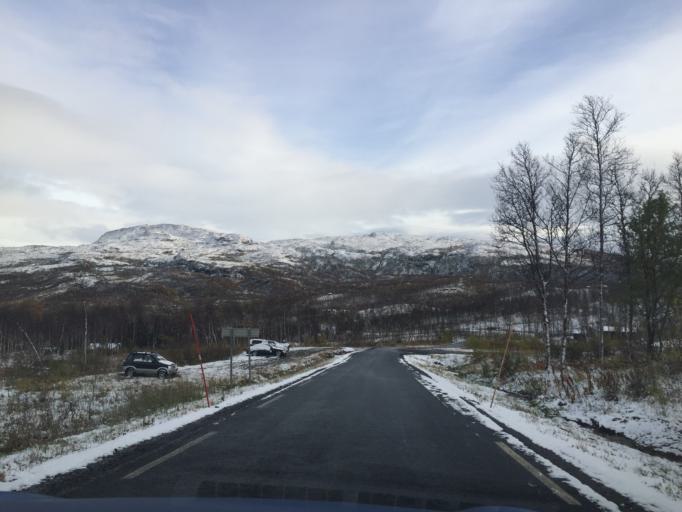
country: NO
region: Nordland
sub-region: Sorfold
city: Straumen
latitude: 67.0853
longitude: 16.0256
